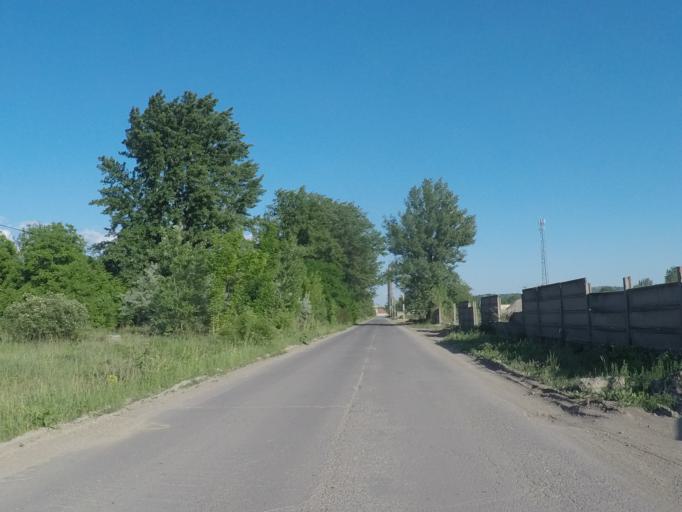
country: HU
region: Borsod-Abauj-Zemplen
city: Mucsony
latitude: 48.2426
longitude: 20.6728
